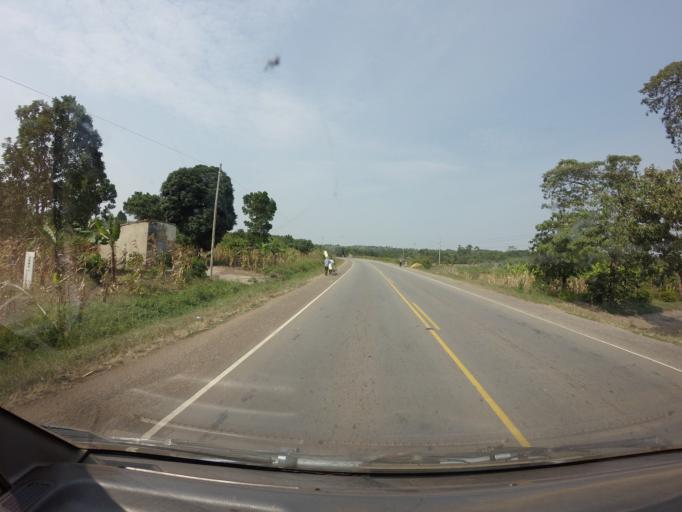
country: UG
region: Central Region
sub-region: Lwengo District
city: Lwengo
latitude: -0.4029
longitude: 31.3880
